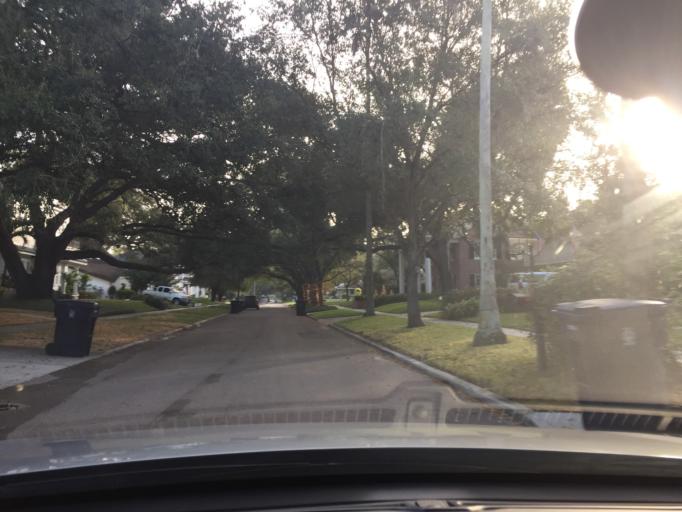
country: US
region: Florida
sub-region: Hillsborough County
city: Tampa
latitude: 27.9368
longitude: -82.4904
